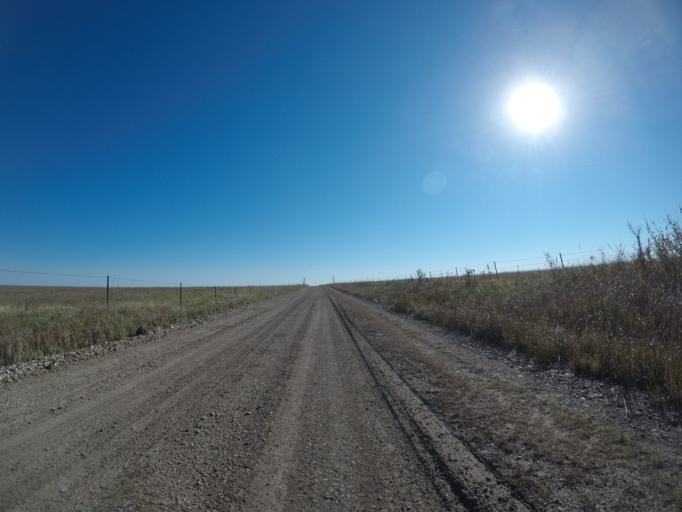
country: US
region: Kansas
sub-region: Wabaunsee County
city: Alma
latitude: 38.8842
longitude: -96.4089
